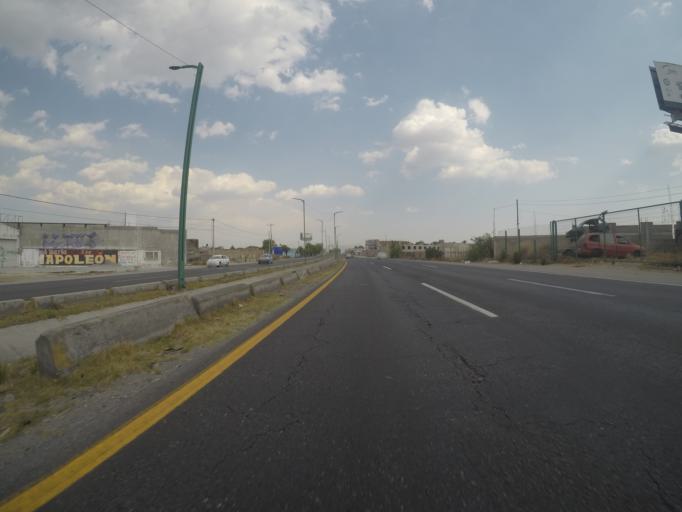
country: MX
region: Mexico
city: San Mateo Mexicaltzingo
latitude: 19.2079
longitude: -99.5909
